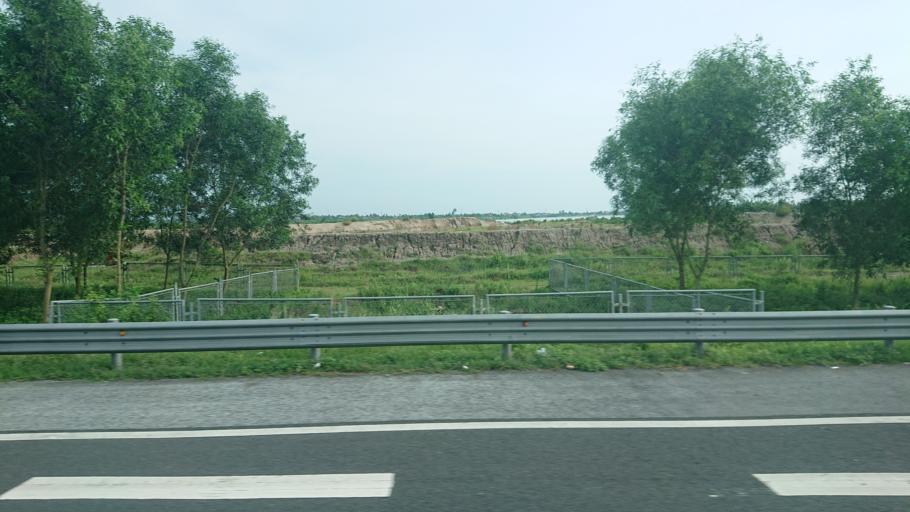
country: VN
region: Hai Phong
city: An Lao
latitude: 20.8012
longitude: 106.5307
